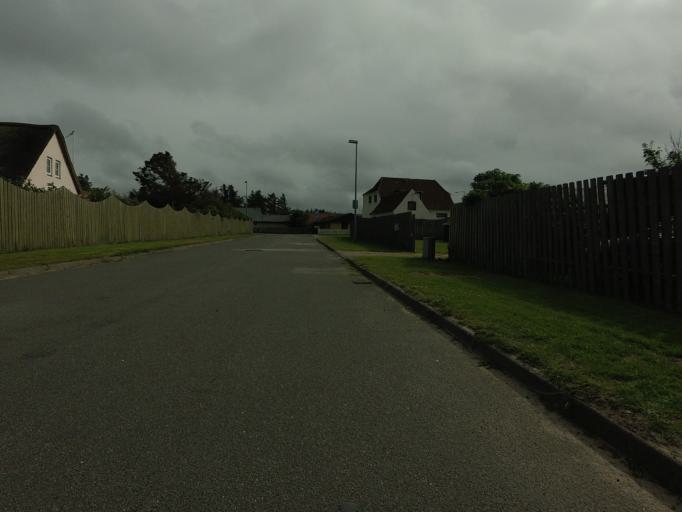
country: DK
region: North Denmark
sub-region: Jammerbugt Kommune
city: Pandrup
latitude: 57.3738
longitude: 9.7184
